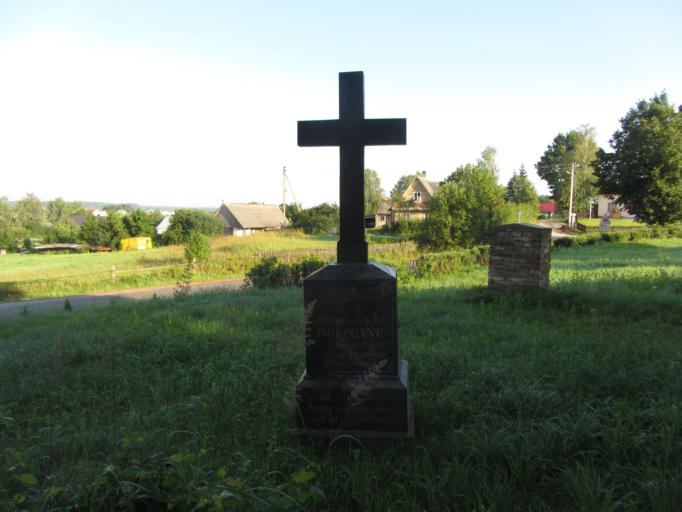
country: LT
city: Trakai
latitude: 54.5011
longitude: 24.9846
